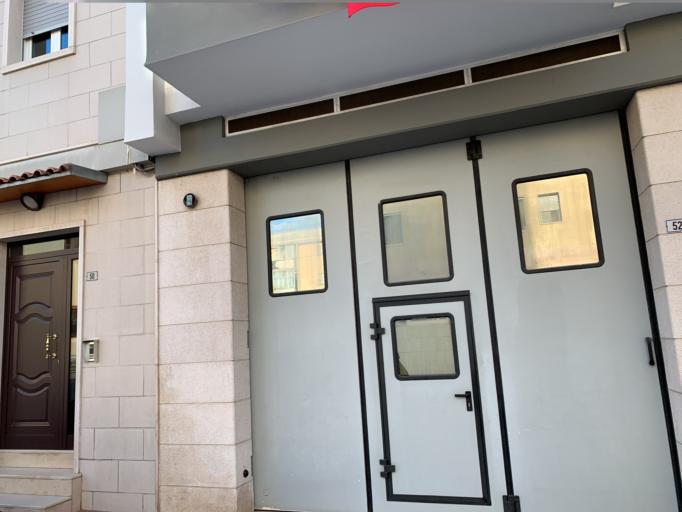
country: IT
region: Apulia
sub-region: Provincia di Barletta - Andria - Trani
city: Andria
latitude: 41.2327
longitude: 16.2878
